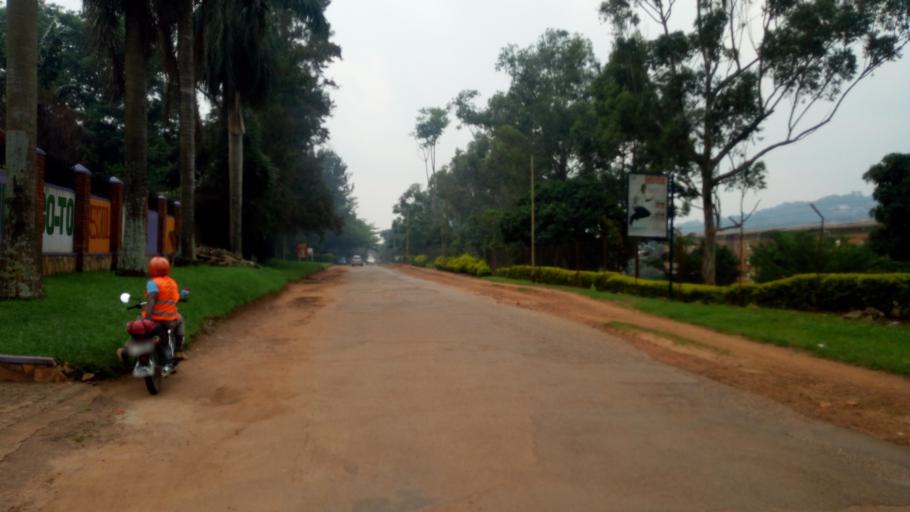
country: UG
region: Central Region
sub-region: Kampala District
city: Kampala
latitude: 0.3119
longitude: 32.6248
